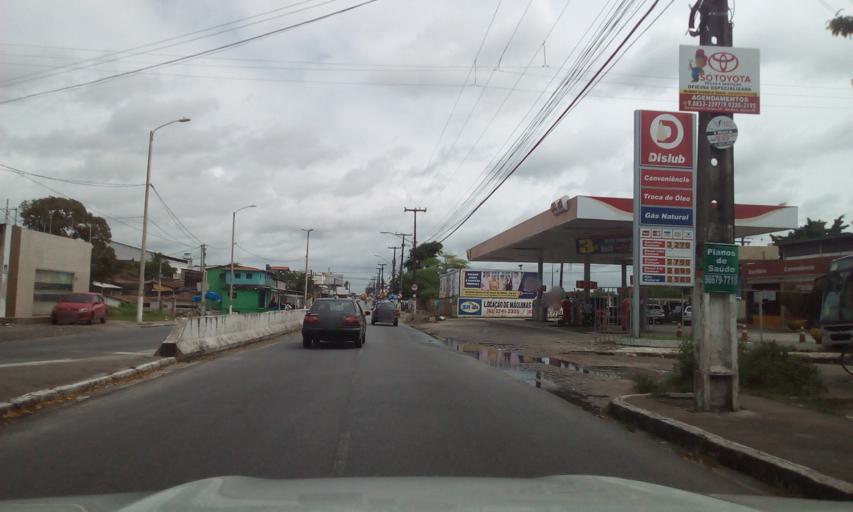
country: BR
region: Paraiba
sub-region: Bayeux
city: Bayeux
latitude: -7.1202
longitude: -34.9046
